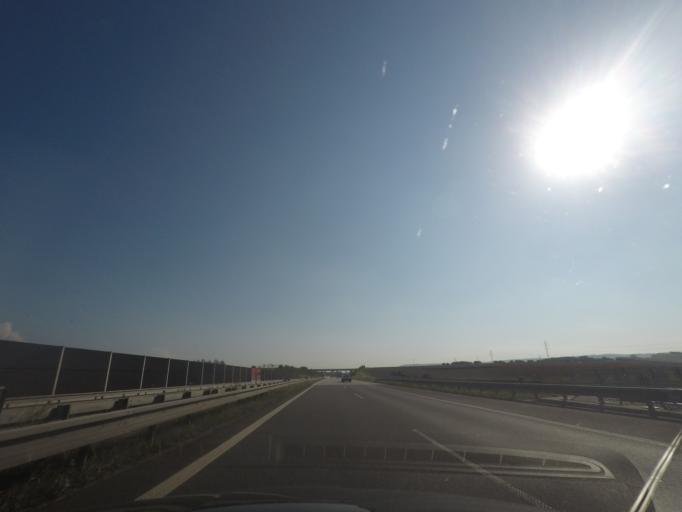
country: CZ
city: Bilovec
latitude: 49.7085
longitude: 17.9947
